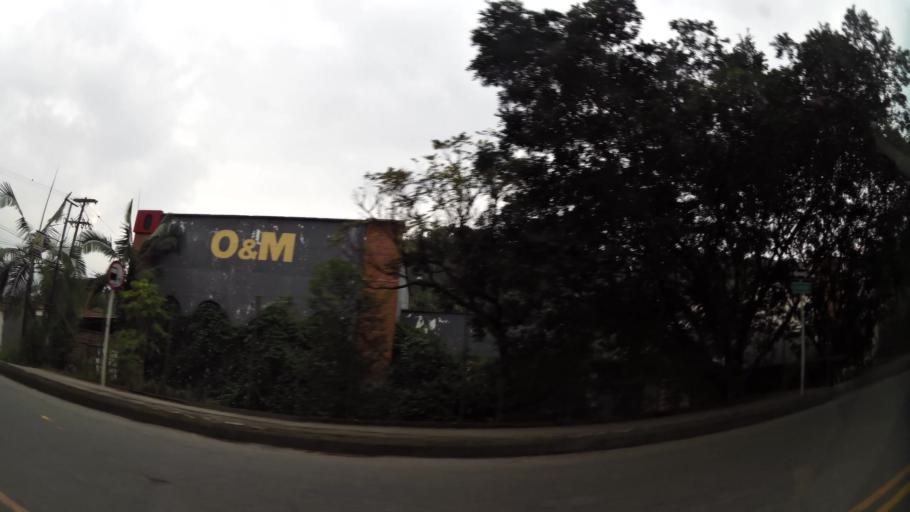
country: CO
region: Antioquia
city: Medellin
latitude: 6.2730
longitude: -75.5847
